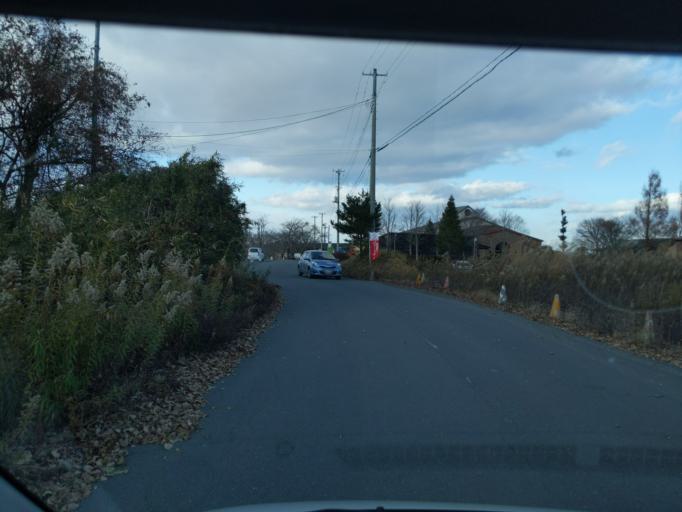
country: JP
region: Miyagi
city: Wakuya
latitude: 38.6983
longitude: 141.1470
